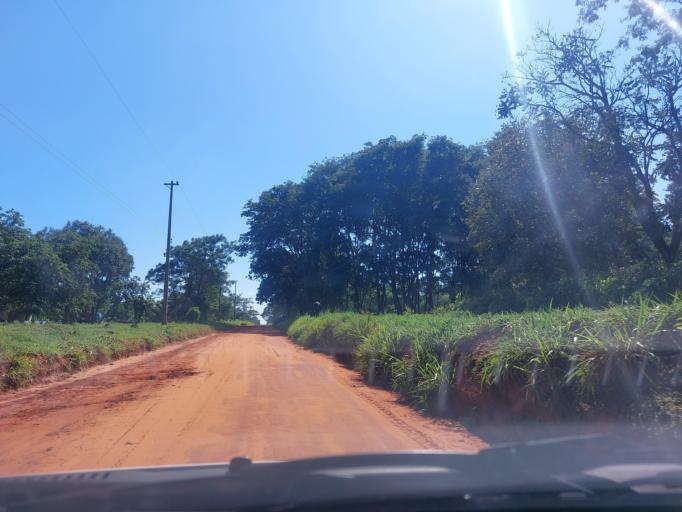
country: PY
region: San Pedro
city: Lima
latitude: -24.1560
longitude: -56.0114
